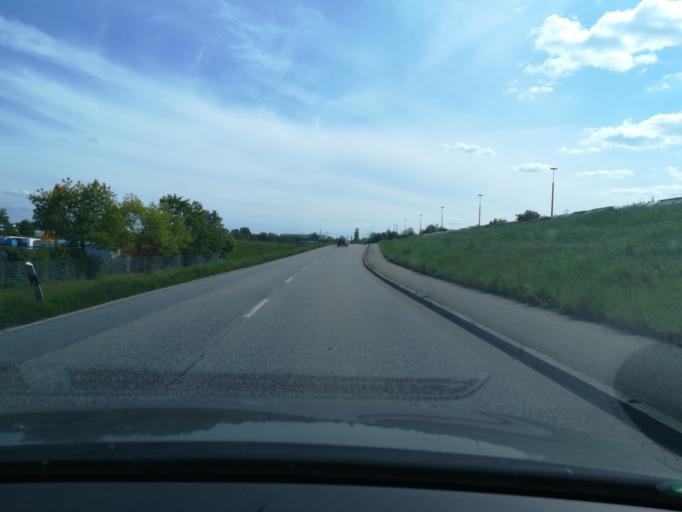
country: DE
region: Hamburg
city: Harburg
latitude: 53.4856
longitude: 9.9873
